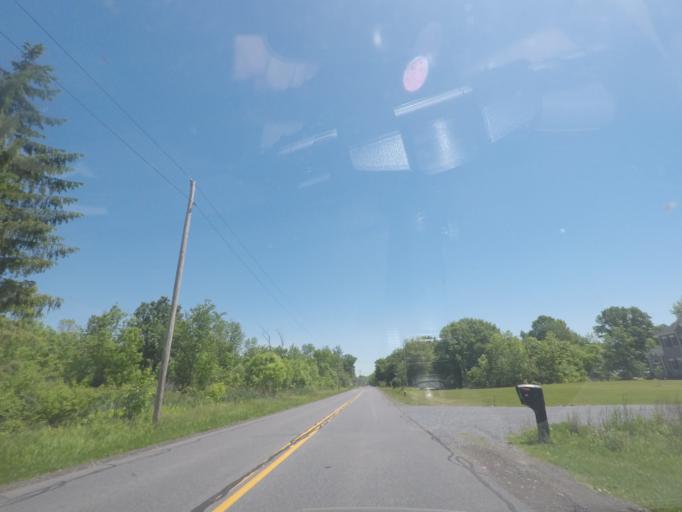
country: US
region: New York
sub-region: Saratoga County
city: Stillwater
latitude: 42.9345
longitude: -73.6735
